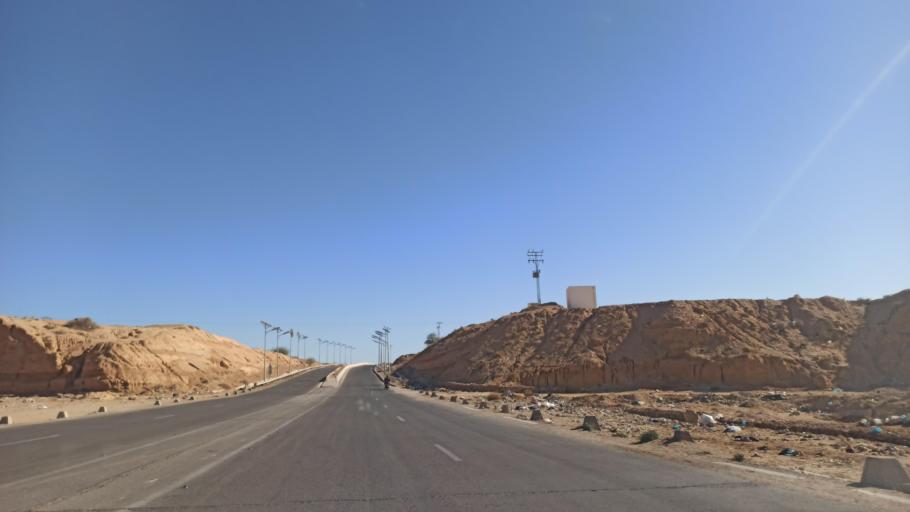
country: TN
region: Gafsa
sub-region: Gafsa Municipality
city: Gafsa
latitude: 34.4333
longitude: 8.8084
